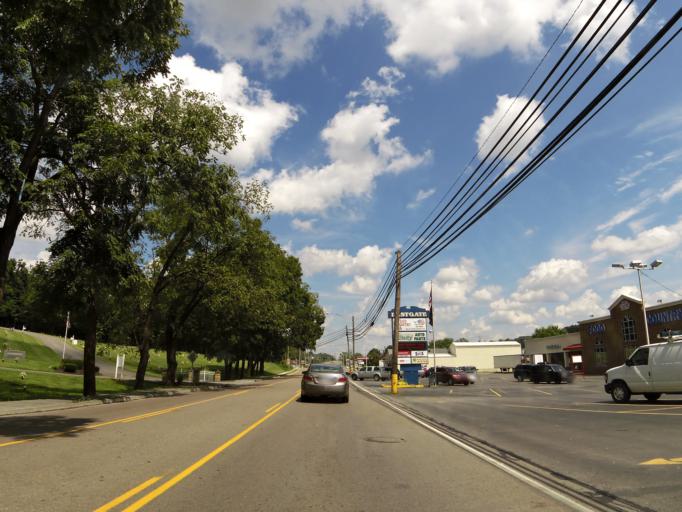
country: US
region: Virginia
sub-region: Washington County
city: Abingdon
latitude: 36.7157
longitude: -81.9593
